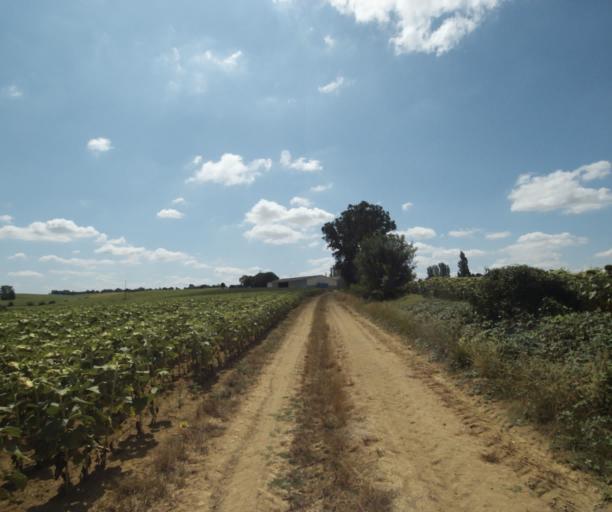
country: FR
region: Midi-Pyrenees
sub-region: Departement de la Haute-Garonne
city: Auriac-sur-Vendinelle
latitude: 43.4697
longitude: 1.8236
